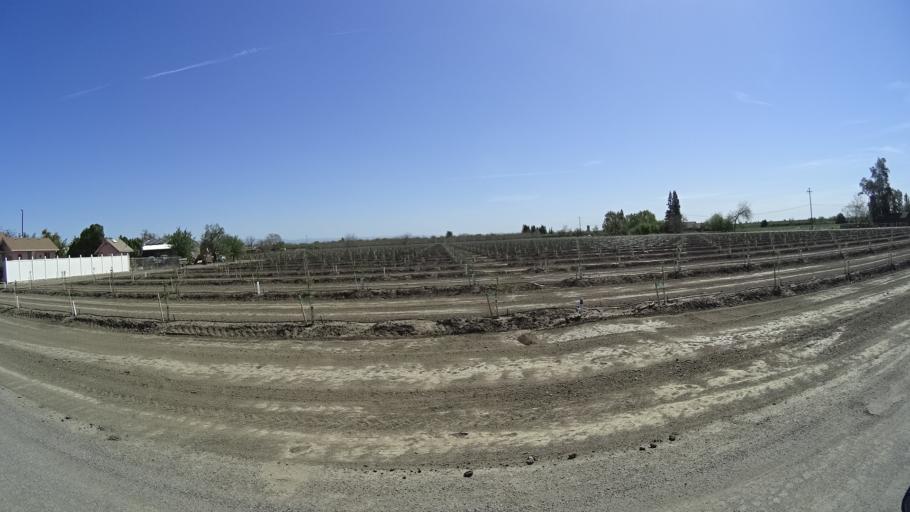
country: US
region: California
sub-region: Glenn County
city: Orland
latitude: 39.7442
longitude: -122.1277
